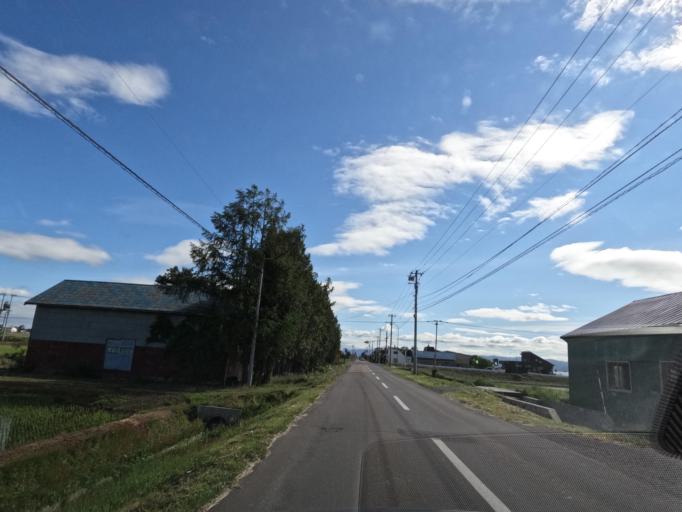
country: JP
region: Hokkaido
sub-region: Asahikawa-shi
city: Asahikawa
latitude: 43.7214
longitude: 142.5241
